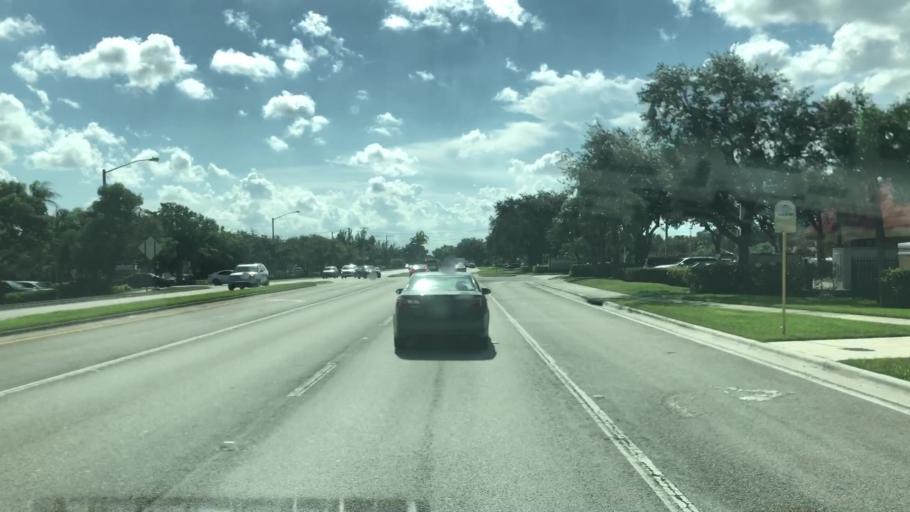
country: US
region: Florida
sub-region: Broward County
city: Parkland
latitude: 26.2870
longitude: -80.2473
